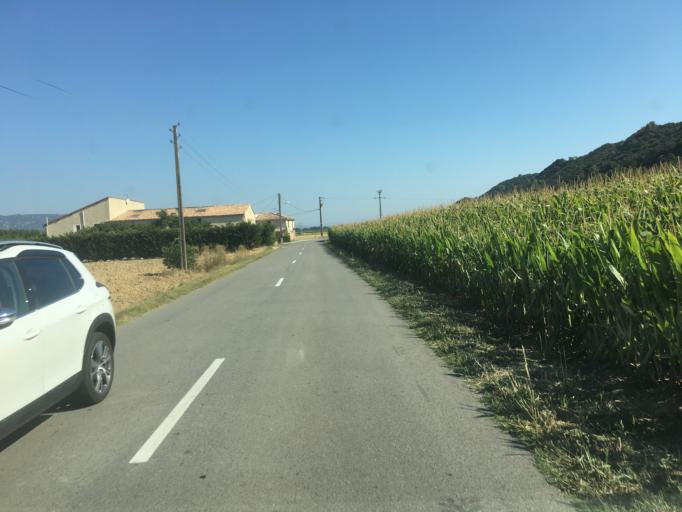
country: FR
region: Provence-Alpes-Cote d'Azur
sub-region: Departement des Alpes-de-Haute-Provence
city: Manosque
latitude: 43.8069
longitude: 5.8426
